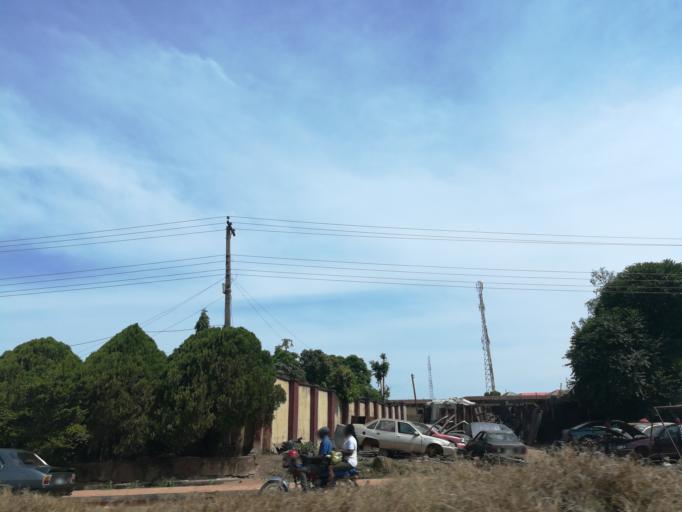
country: NG
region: Plateau
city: Bukuru
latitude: 9.7915
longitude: 8.8593
